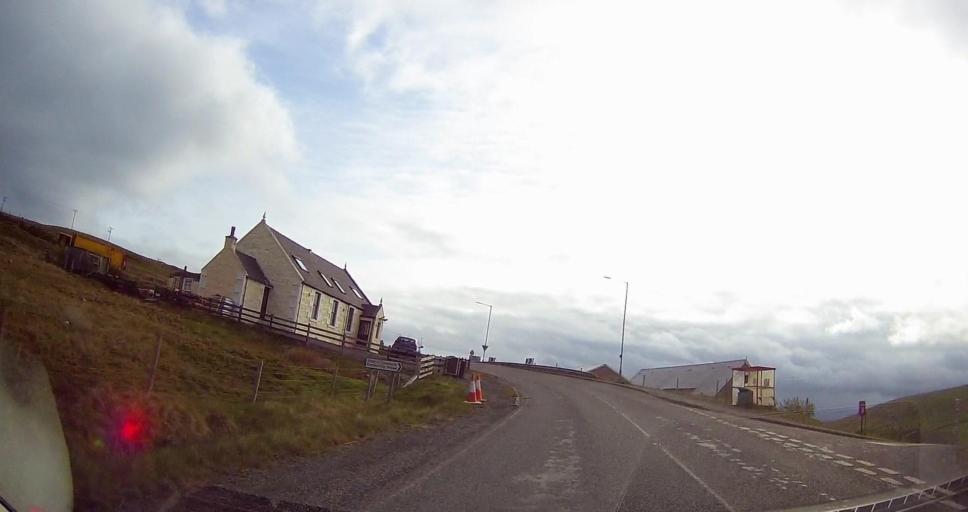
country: GB
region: Scotland
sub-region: Shetland Islands
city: Lerwick
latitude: 60.4460
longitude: -1.2061
